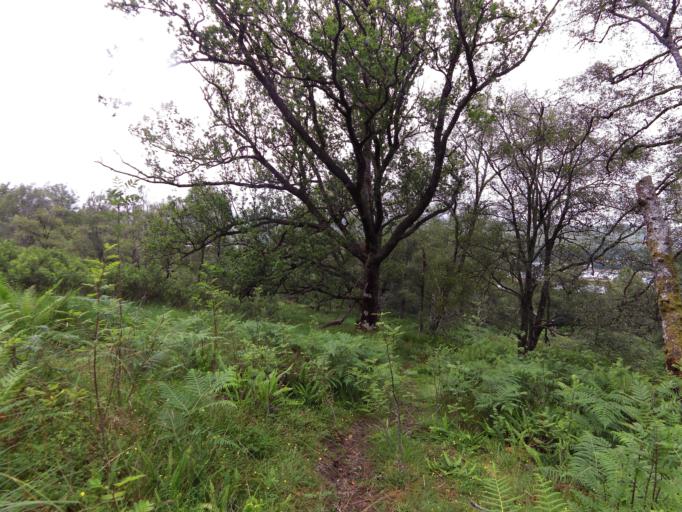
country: GB
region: Scotland
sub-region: Highland
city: Fort William
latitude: 56.8319
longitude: -5.1307
